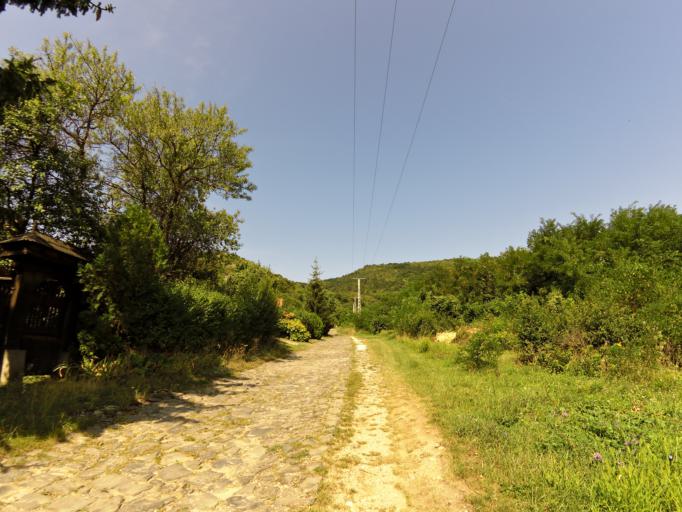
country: HU
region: Zala
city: Vonyarcvashegy
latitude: 46.7887
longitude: 17.3692
